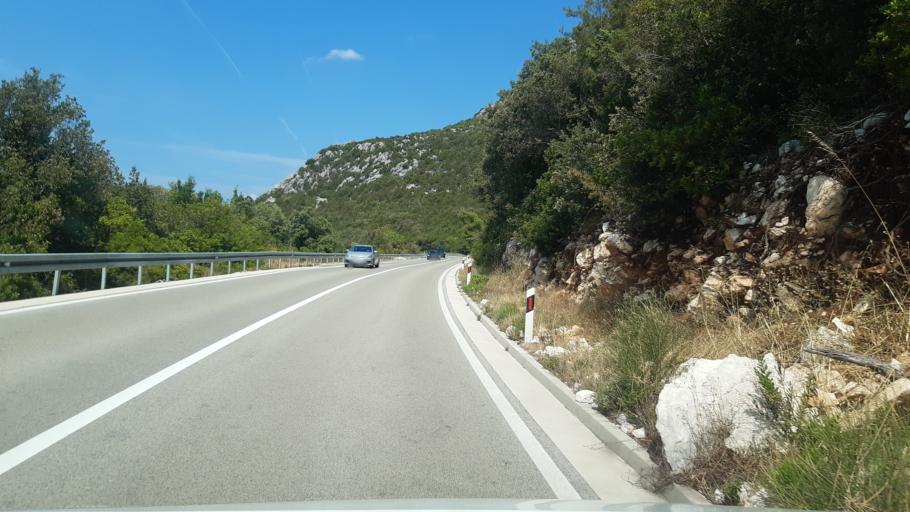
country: HR
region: Dubrovacko-Neretvanska
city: Ston
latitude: 42.8444
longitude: 17.7291
